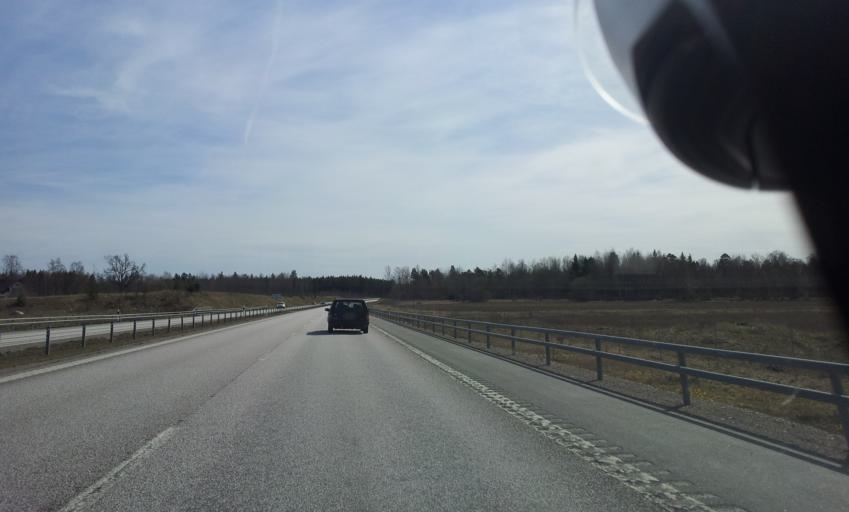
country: SE
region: Uppsala
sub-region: Tierps Kommun
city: Tierp
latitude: 60.3227
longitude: 17.5134
